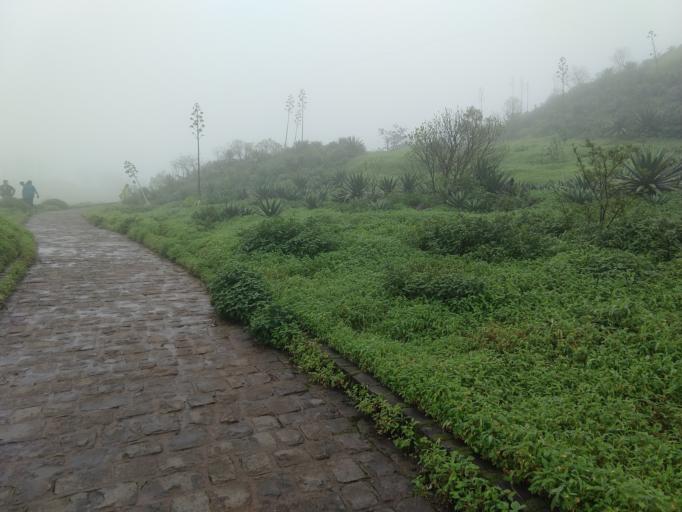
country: IN
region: Maharashtra
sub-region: Pune Division
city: Kharakvasla
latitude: 18.3651
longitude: 73.7536
